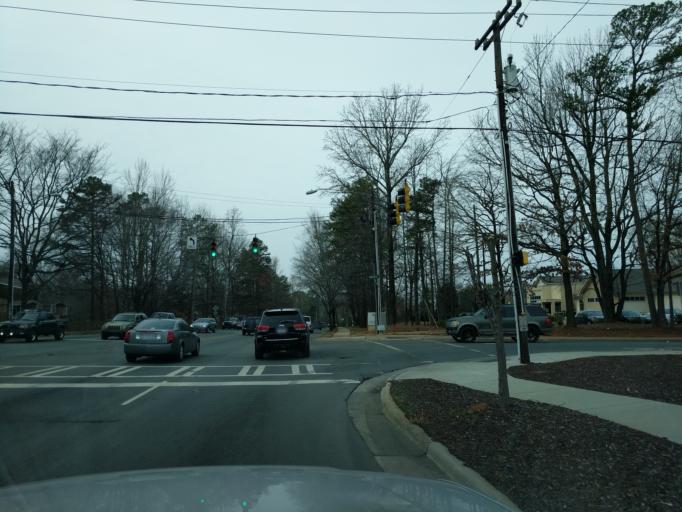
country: US
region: North Carolina
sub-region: Mecklenburg County
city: Charlotte
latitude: 35.1902
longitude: -80.7981
